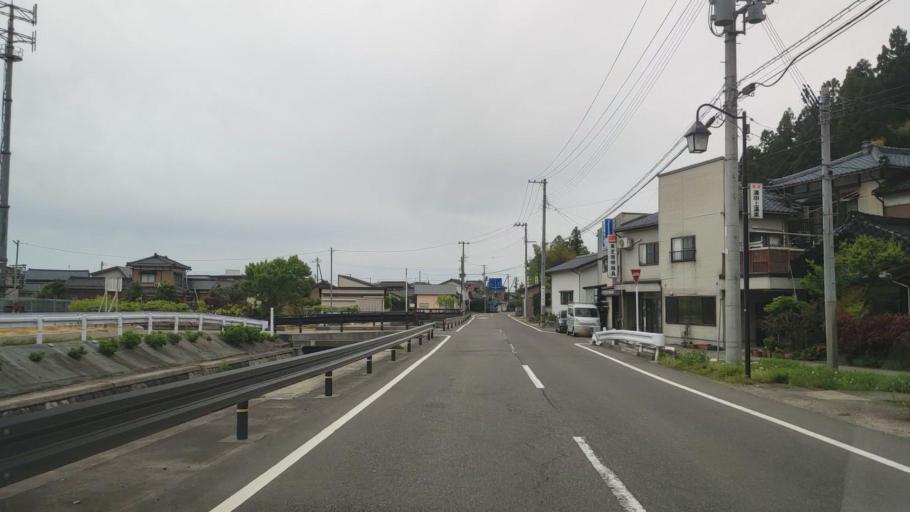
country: JP
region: Niigata
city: Kamo
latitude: 37.7118
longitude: 139.0769
